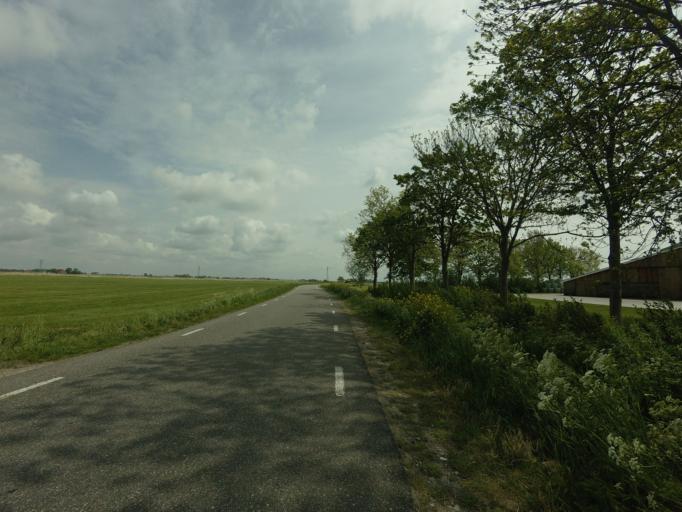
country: NL
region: Friesland
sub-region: Sudwest Fryslan
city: Bolsward
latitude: 53.1077
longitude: 5.4960
